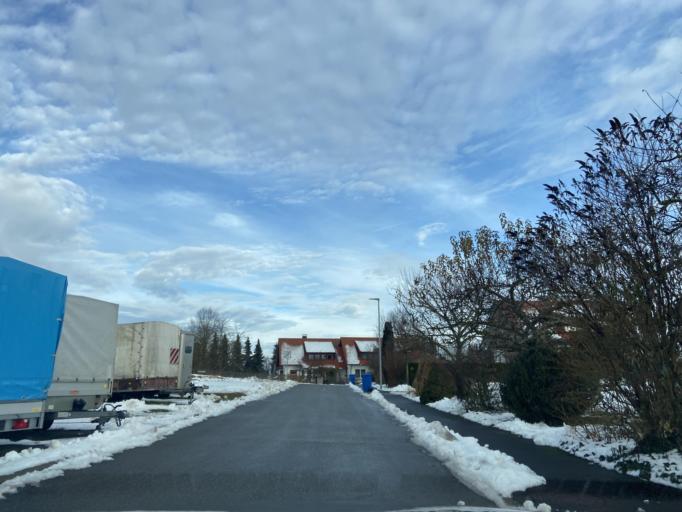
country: DE
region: Baden-Wuerttemberg
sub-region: Tuebingen Region
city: Hettingen
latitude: 48.1934
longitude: 9.2831
